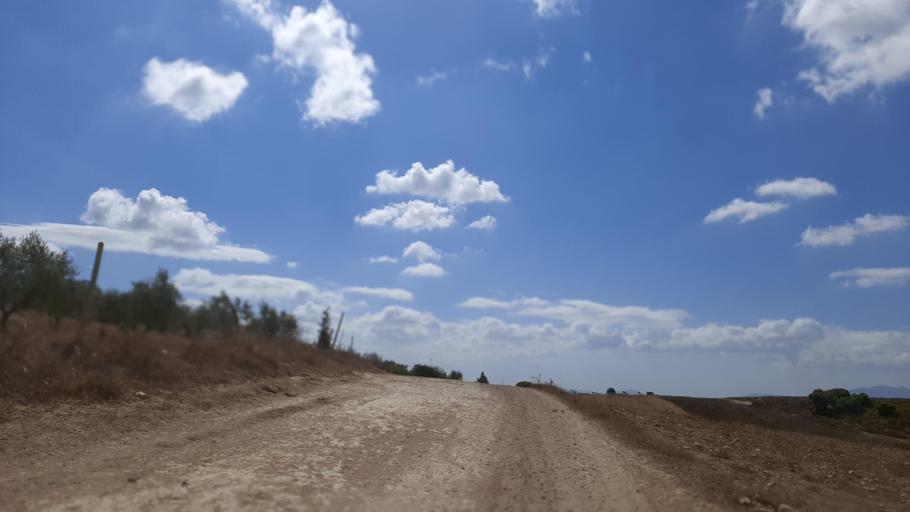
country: TN
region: Zaghwan
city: Zaghouan
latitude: 36.4859
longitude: 10.1804
